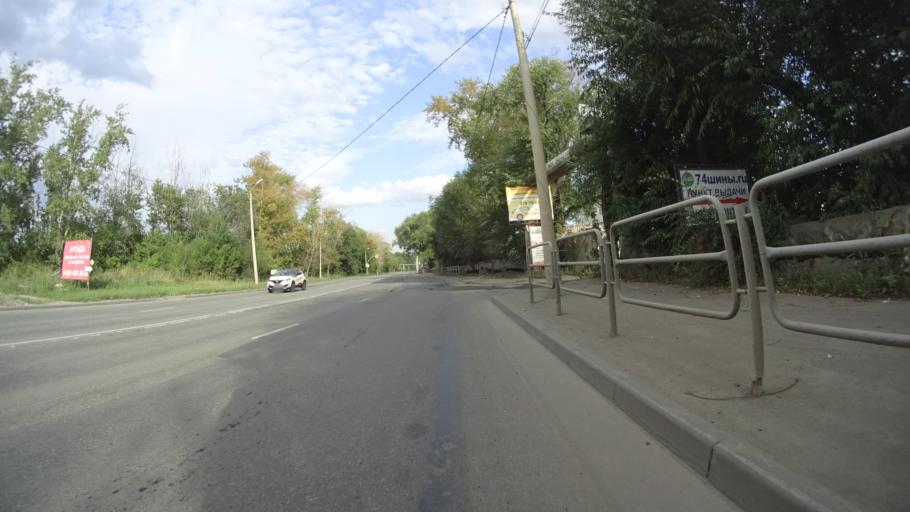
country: RU
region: Chelyabinsk
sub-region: Gorod Chelyabinsk
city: Chelyabinsk
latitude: 55.1960
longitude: 61.3769
